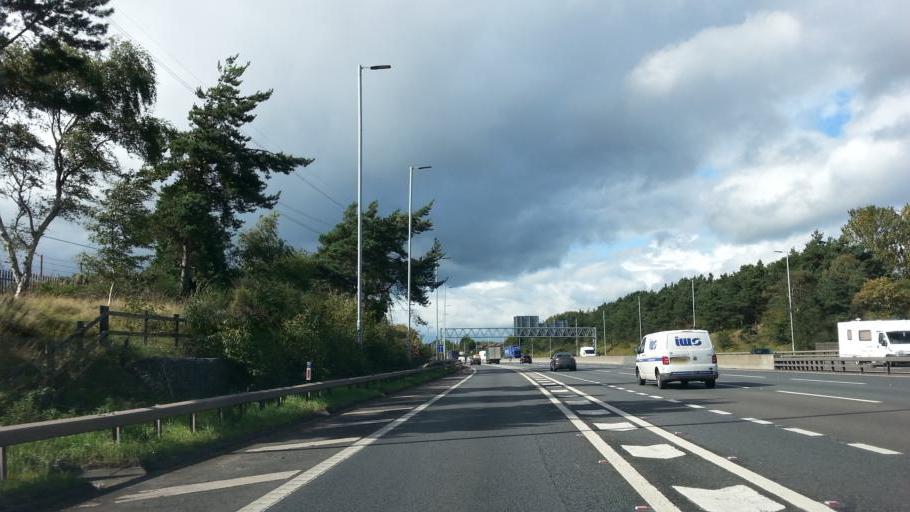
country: GB
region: England
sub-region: City and Borough of Birmingham
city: Birmingham
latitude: 52.5150
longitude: -1.8683
